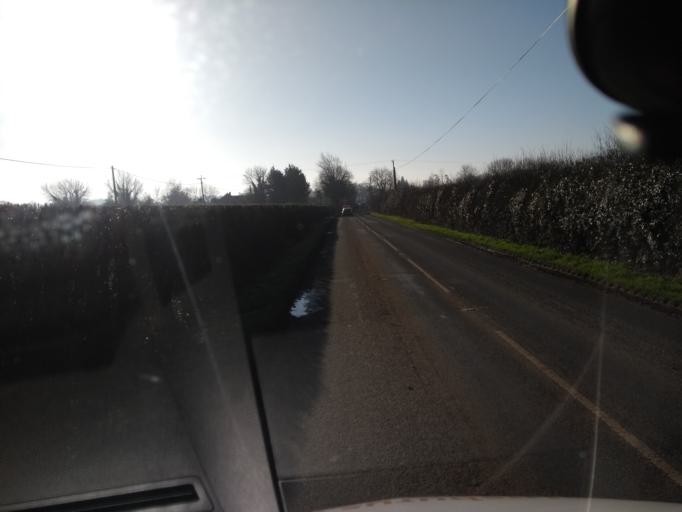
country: GB
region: England
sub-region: Somerset
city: Wincanton
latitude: 51.0749
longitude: -2.4122
